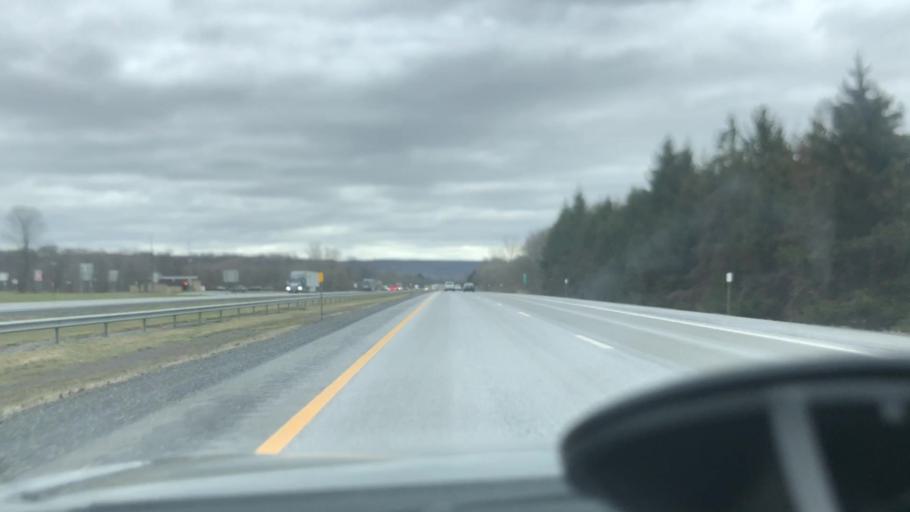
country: US
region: New York
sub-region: Herkimer County
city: Frankfort
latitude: 43.0758
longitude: -75.1037
